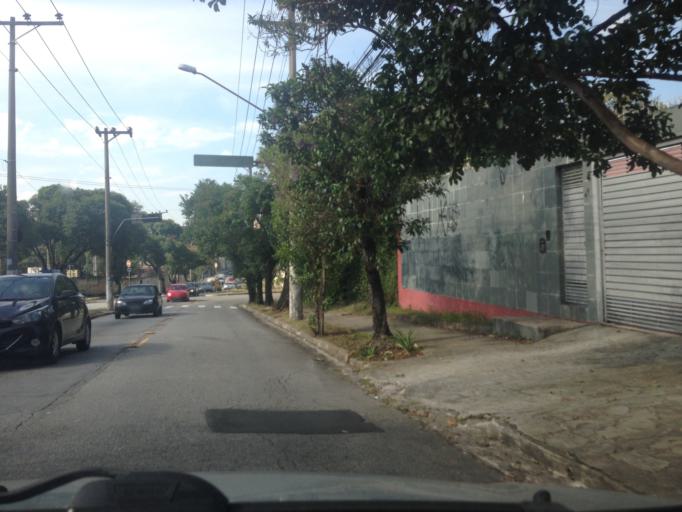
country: BR
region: Sao Paulo
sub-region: Osasco
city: Osasco
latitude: -23.5208
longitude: -46.7131
